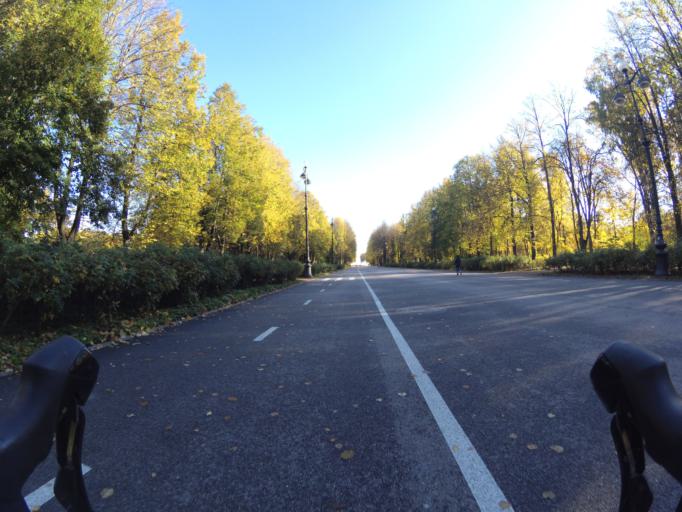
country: RU
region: St.-Petersburg
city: Staraya Derevnya
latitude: 59.9724
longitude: 30.2345
